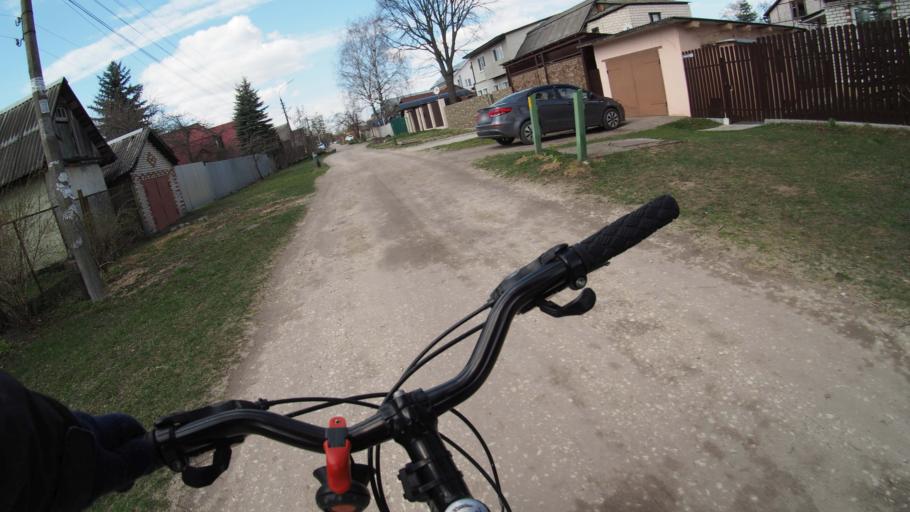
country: RU
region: Moskovskaya
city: Ramenskoye
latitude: 55.5610
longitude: 38.2236
